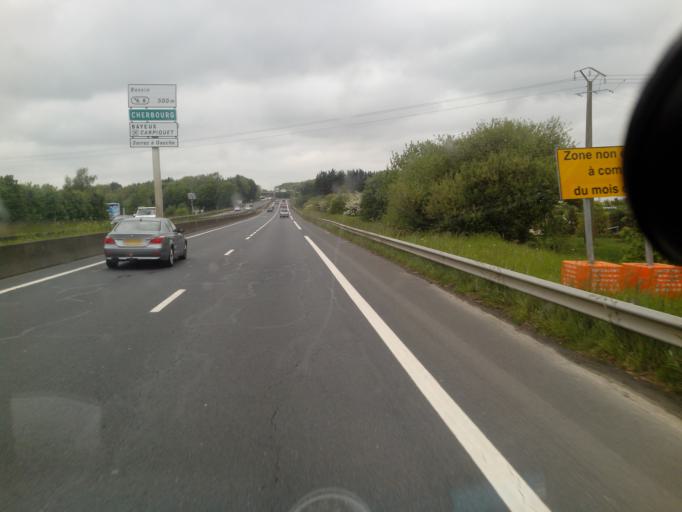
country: FR
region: Lower Normandy
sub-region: Departement du Calvados
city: Bretteville-sur-Odon
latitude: 49.1821
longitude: -0.4260
